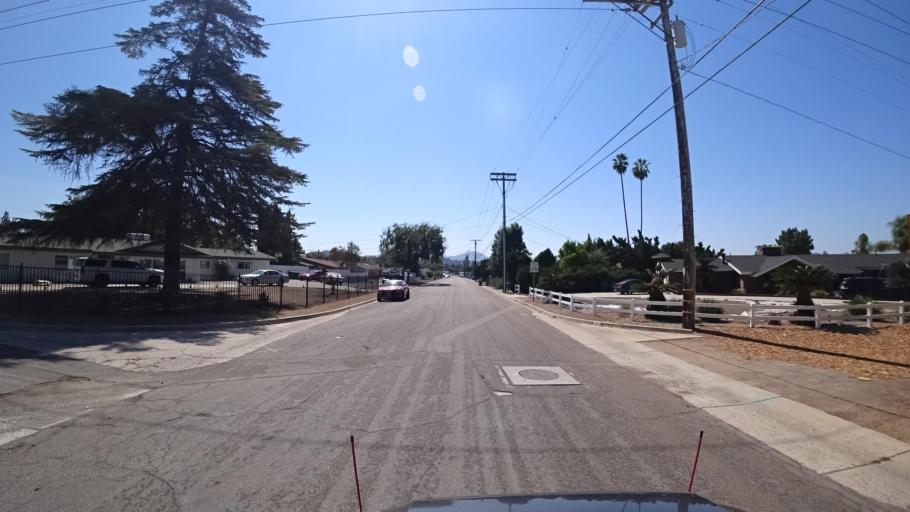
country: US
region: California
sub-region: San Diego County
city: Granite Hills
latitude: 32.8041
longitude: -116.9197
